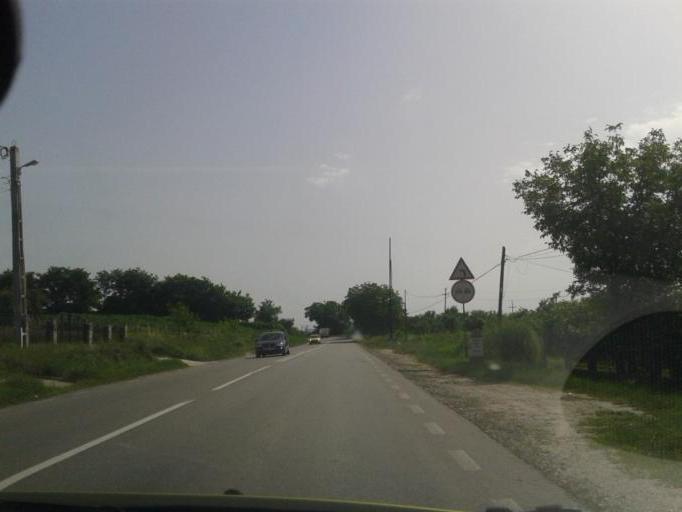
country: RO
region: Valcea
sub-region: Comuna Mihaesti
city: Mihaesti
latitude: 45.0443
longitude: 24.2681
